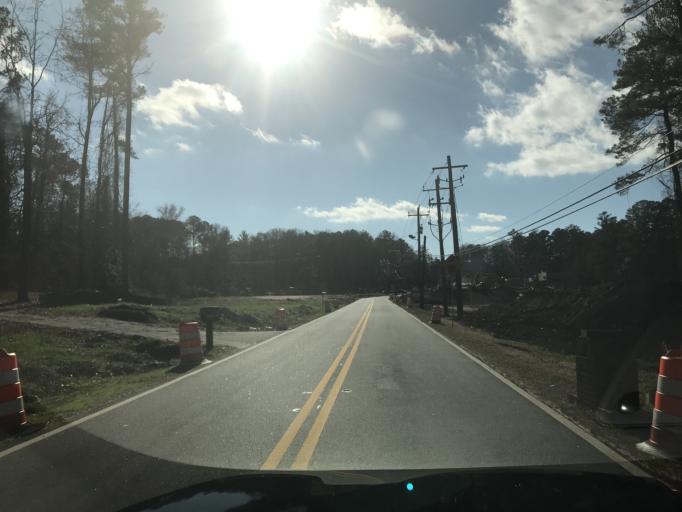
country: US
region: Georgia
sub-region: Cobb County
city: Mableton
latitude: 33.7101
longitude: -84.5575
